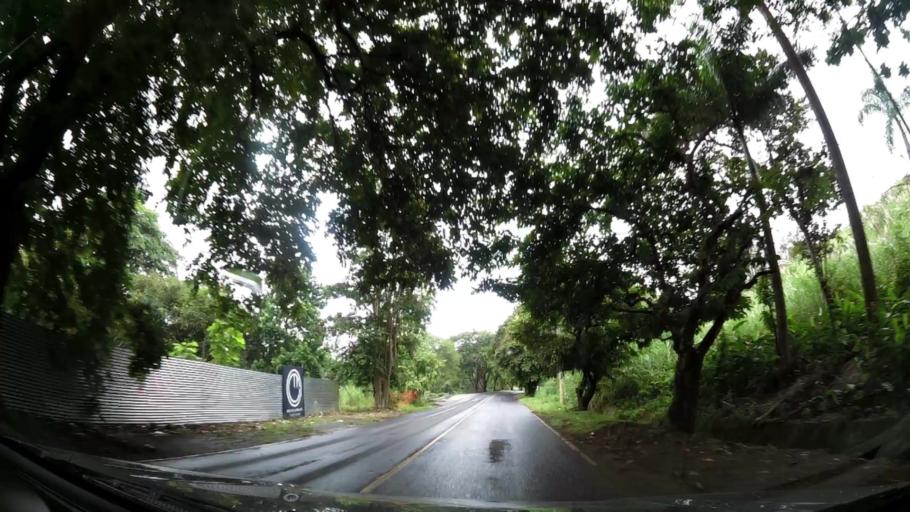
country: PA
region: Panama
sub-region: Distrito de Panama
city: Ancon
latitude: 8.9900
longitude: -79.5553
